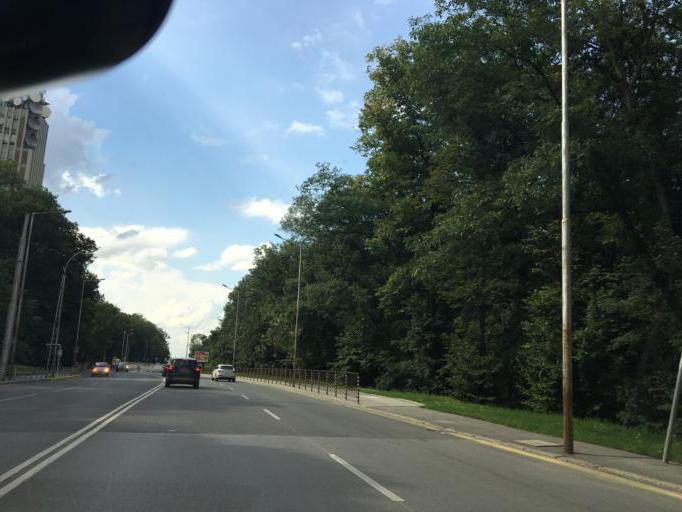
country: BG
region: Sofia-Capital
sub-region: Stolichna Obshtina
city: Sofia
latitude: 42.6760
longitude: 23.3437
